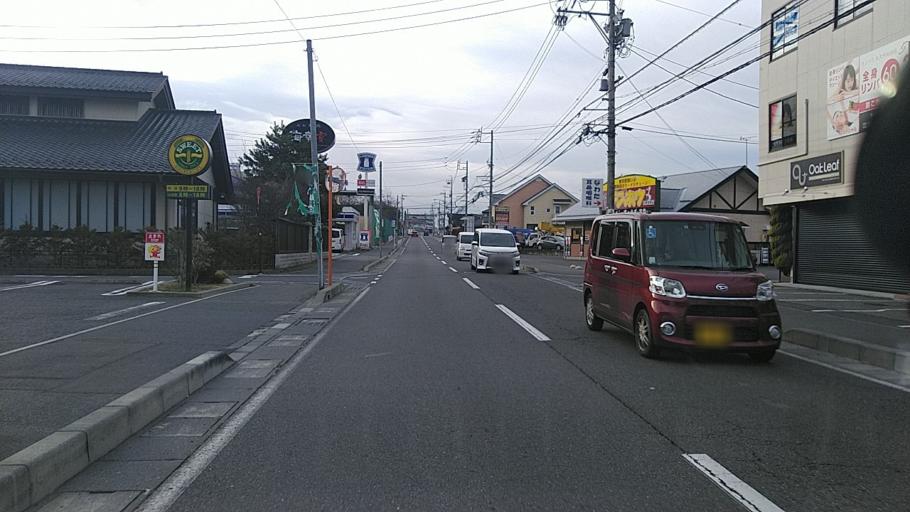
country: JP
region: Nagano
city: Matsumoto
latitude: 36.2094
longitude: 137.9794
